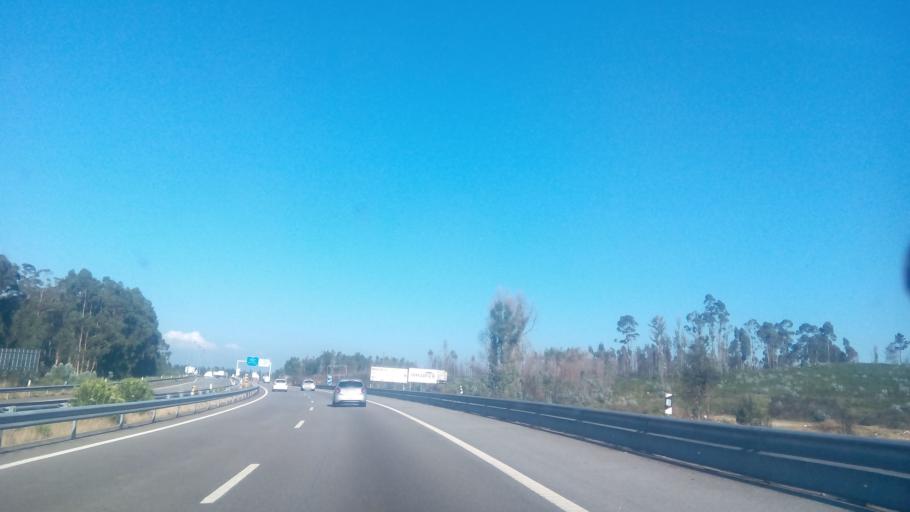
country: PT
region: Porto
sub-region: Pacos de Ferreira
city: Pacos de Ferreira
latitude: 41.2598
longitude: -8.3712
